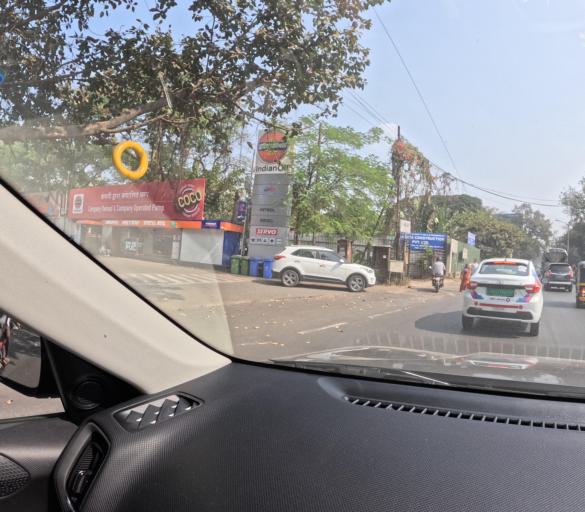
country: IN
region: Maharashtra
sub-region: Pune Division
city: Pune
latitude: 18.5265
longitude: 73.8657
